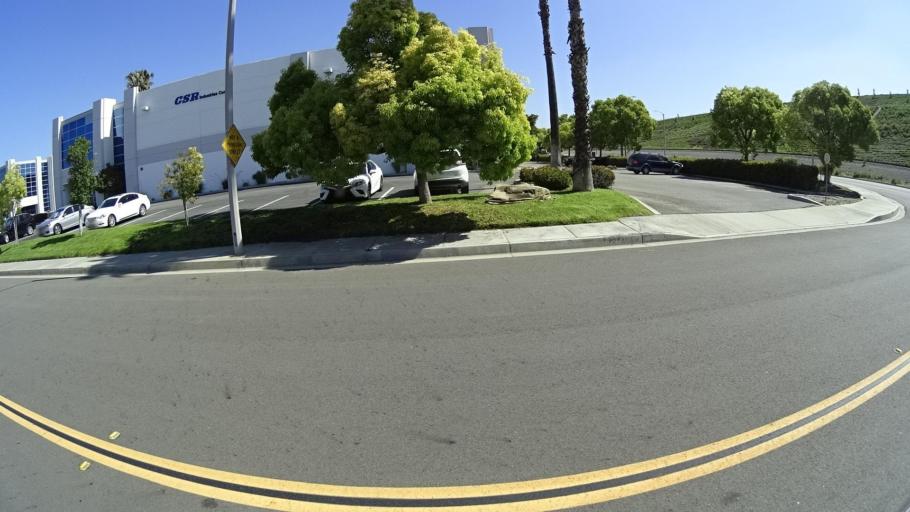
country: US
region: California
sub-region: Los Angeles County
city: Diamond Bar
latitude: 34.0249
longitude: -117.8284
